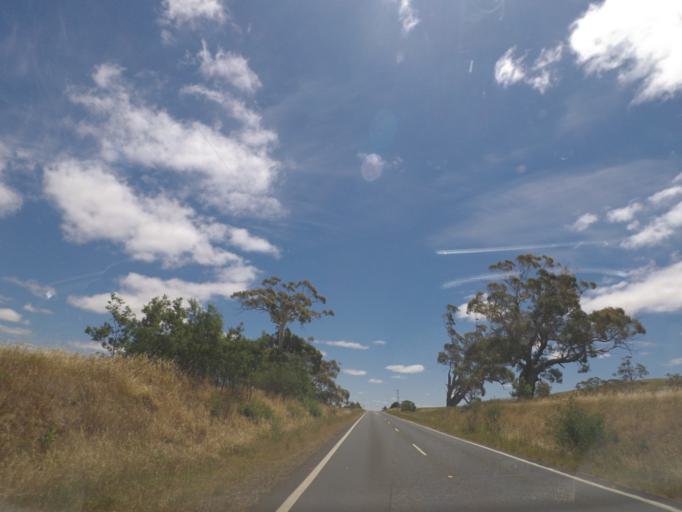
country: AU
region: Victoria
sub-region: Mount Alexander
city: Castlemaine
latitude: -37.2701
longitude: 144.1427
